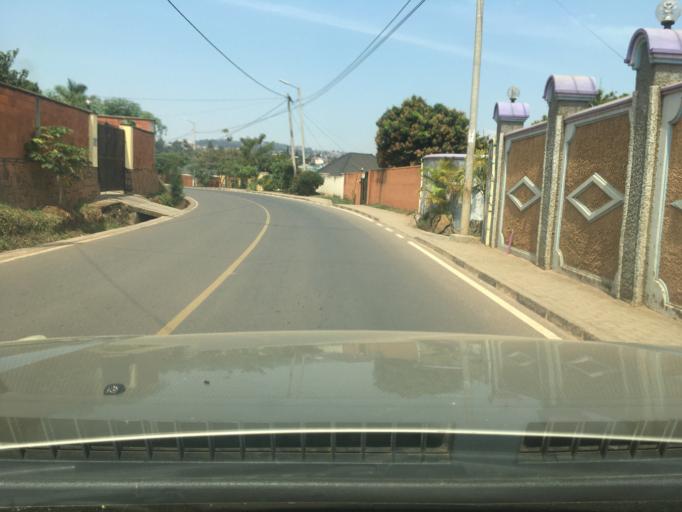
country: RW
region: Kigali
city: Kigali
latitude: -1.9644
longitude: 30.1013
